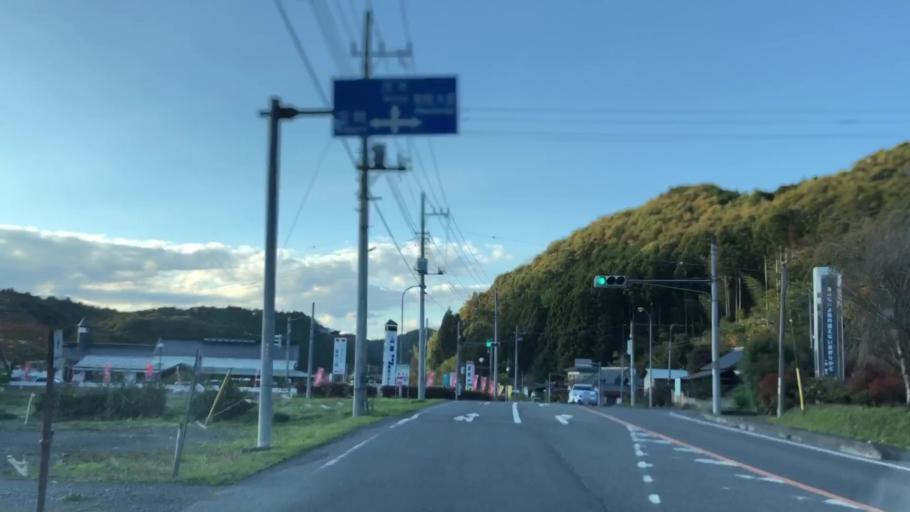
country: JP
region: Ibaraki
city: Kasama
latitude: 36.4776
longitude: 140.3013
